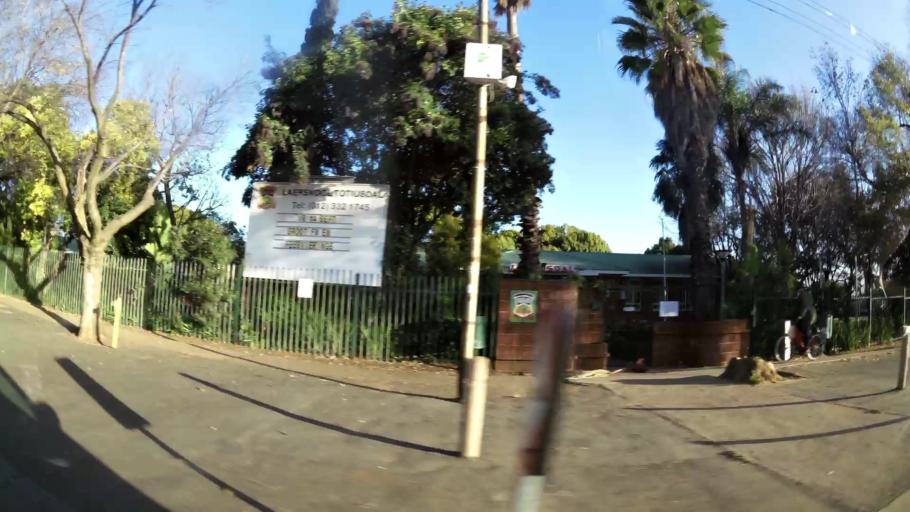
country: ZA
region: Gauteng
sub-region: City of Tshwane Metropolitan Municipality
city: Pretoria
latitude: -25.7015
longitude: 28.2462
